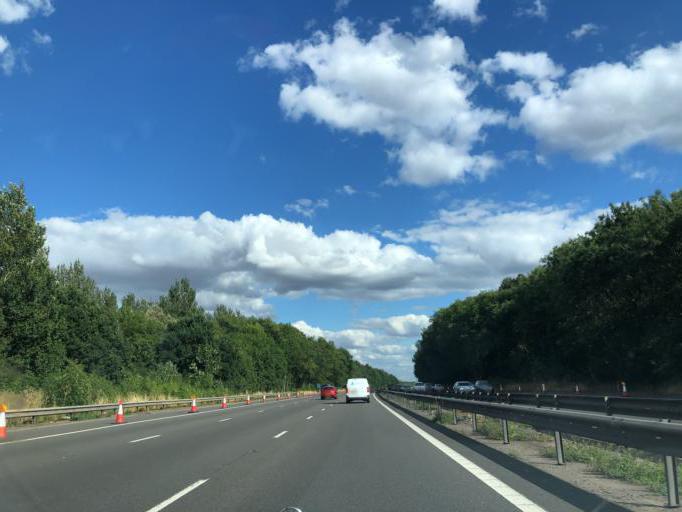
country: GB
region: England
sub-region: Milton Keynes
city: Gayhurst
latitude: 52.1025
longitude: -0.7714
